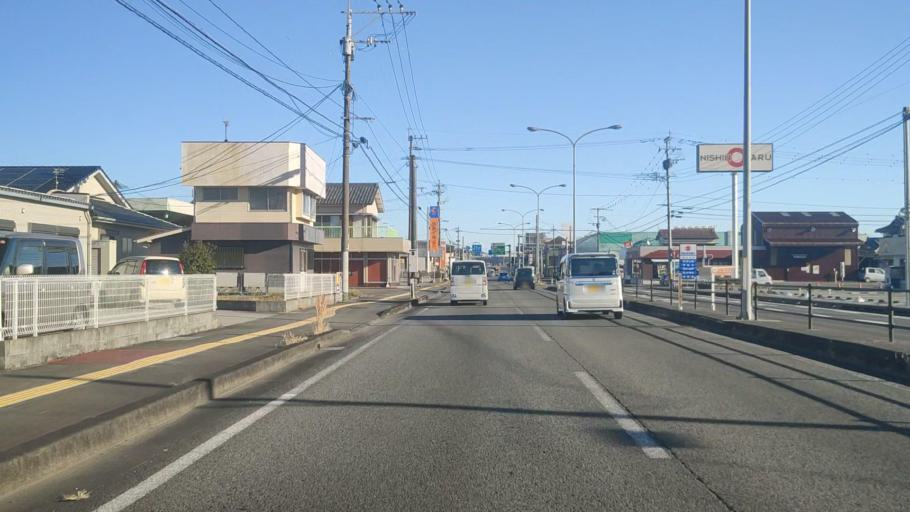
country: JP
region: Miyazaki
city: Nobeoka
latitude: 32.4694
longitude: 131.6495
